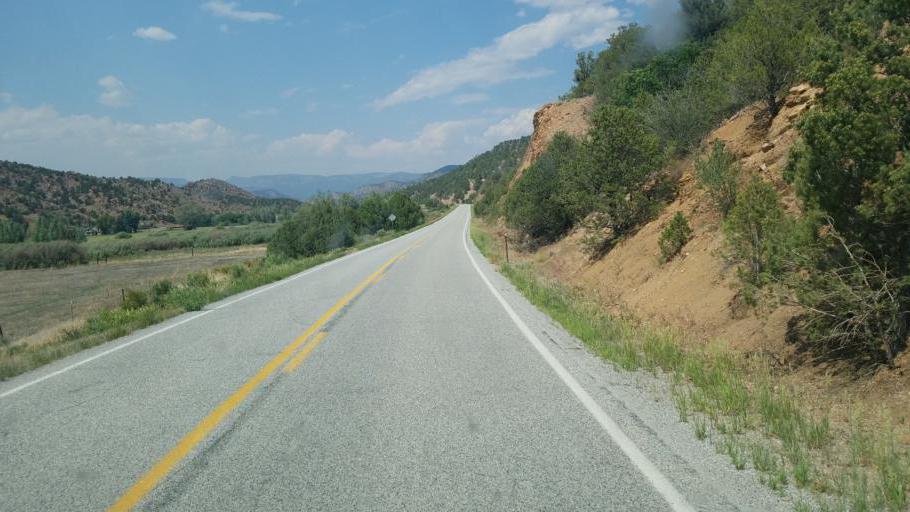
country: US
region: Colorado
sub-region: Custer County
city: Westcliffe
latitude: 38.3517
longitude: -105.5937
